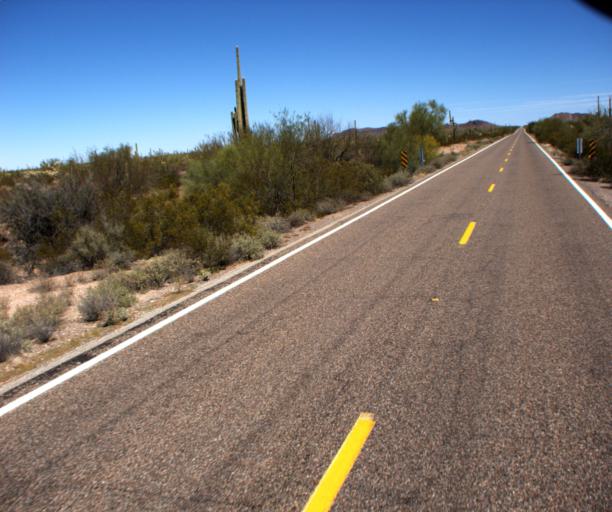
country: MX
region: Sonora
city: Sonoyta
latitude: 32.0508
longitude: -112.7911
